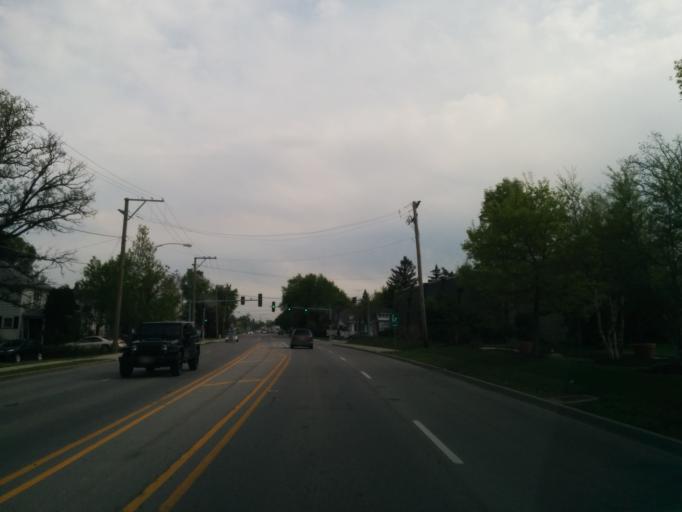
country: US
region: Illinois
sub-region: Kane County
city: North Aurora
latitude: 41.8089
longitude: -88.3279
